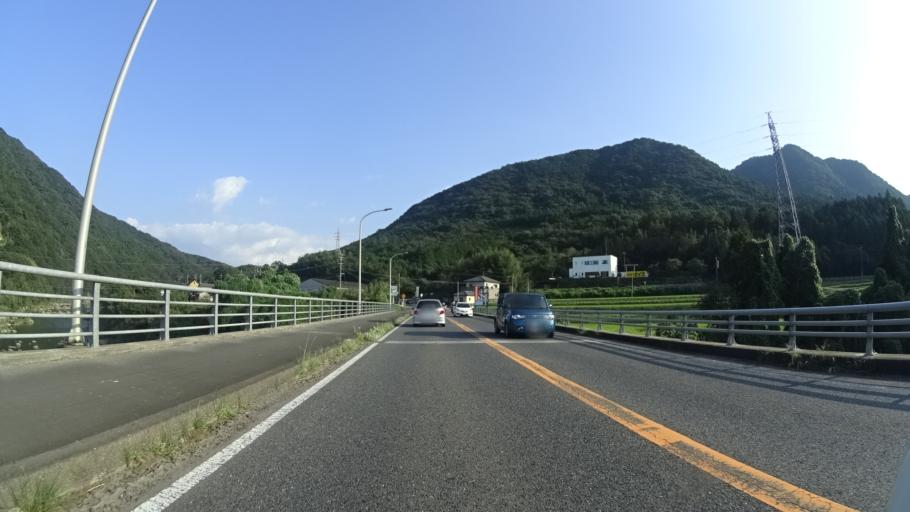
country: JP
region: Oita
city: Bungo-Takada-shi
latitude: 33.4920
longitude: 131.3284
